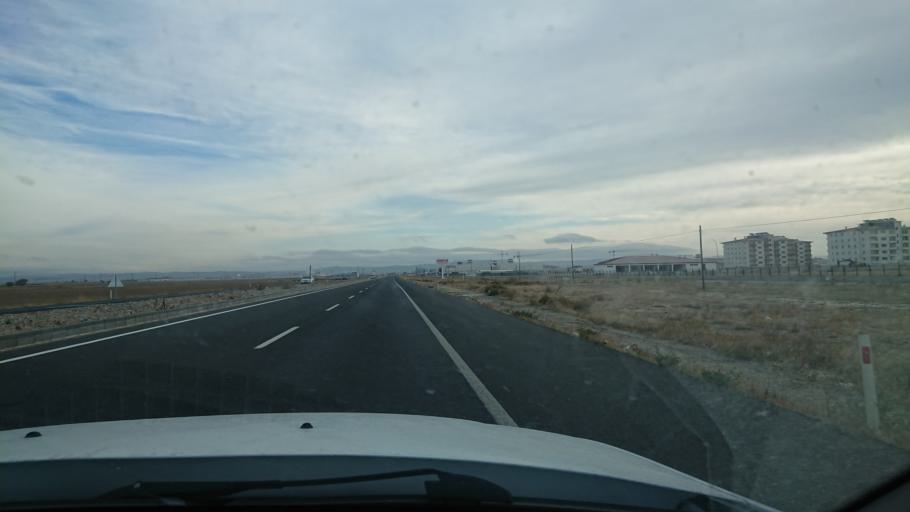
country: TR
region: Aksaray
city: Yesilova
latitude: 38.3328
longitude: 33.9172
